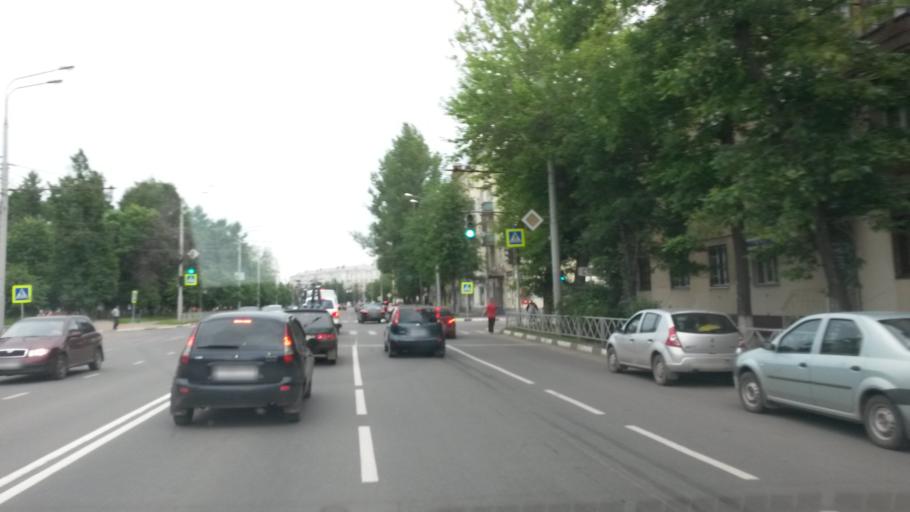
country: RU
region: Jaroslavl
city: Yaroslavl
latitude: 57.6309
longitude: 39.8591
